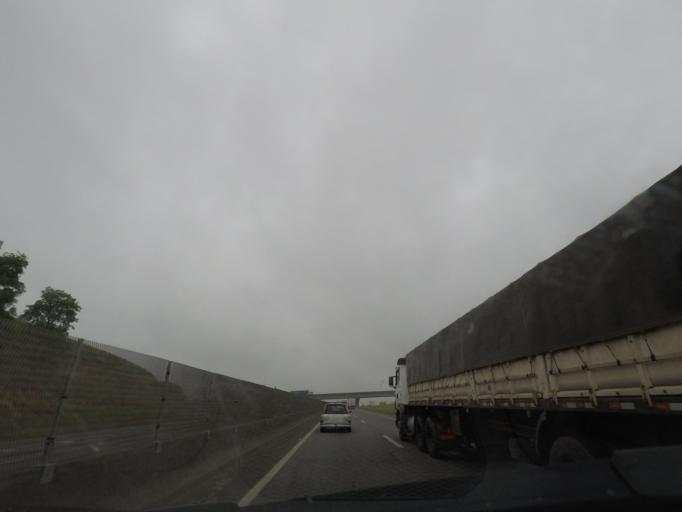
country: BR
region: Sao Paulo
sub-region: Taubate
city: Taubate
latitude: -23.0607
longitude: -45.6228
